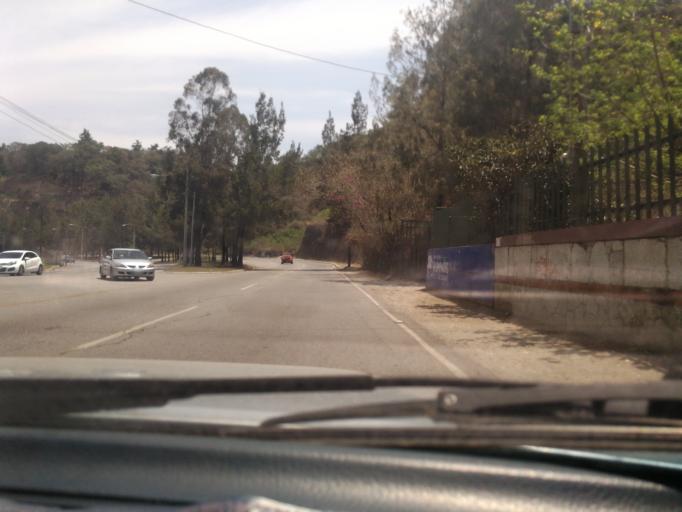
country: GT
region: Guatemala
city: Guatemala City
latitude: 14.6223
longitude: -90.4889
